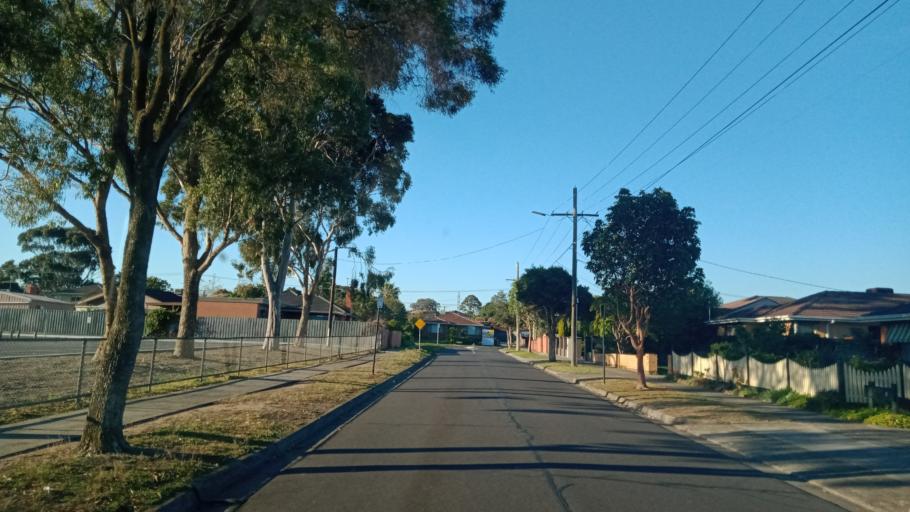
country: AU
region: Victoria
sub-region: Greater Dandenong
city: Springvale
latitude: -37.9327
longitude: 145.1710
